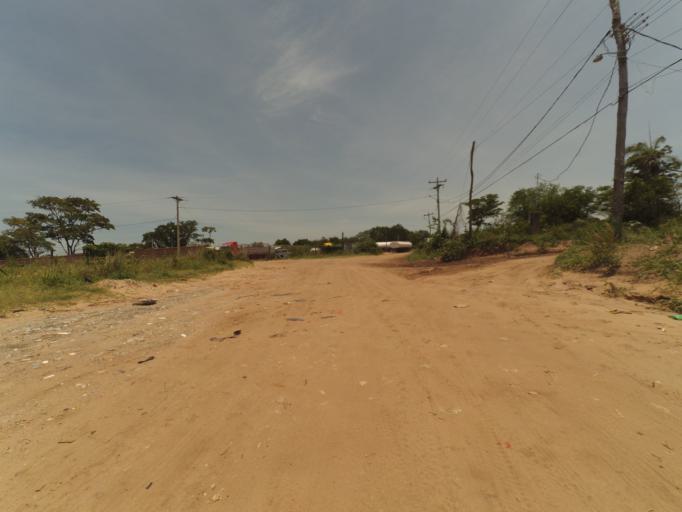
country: BO
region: Santa Cruz
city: Santa Cruz de la Sierra
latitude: -17.8305
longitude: -63.2520
